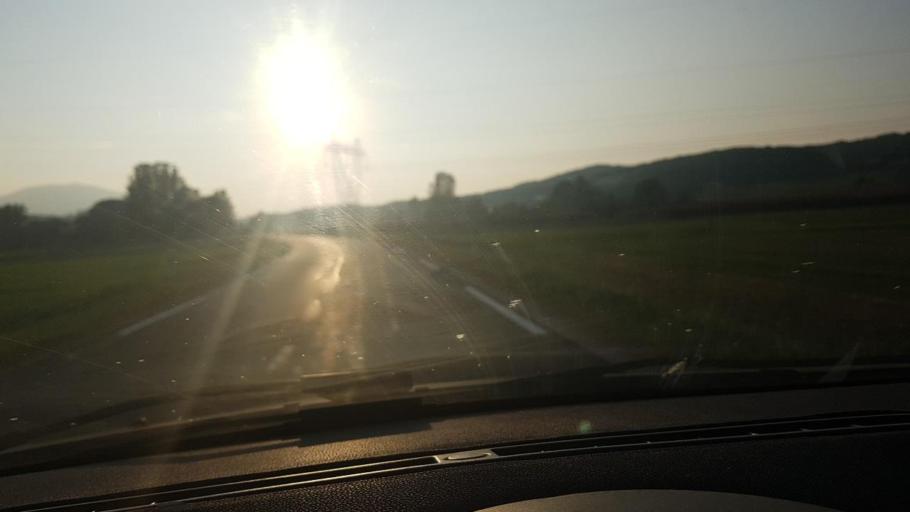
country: SI
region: Majsperk
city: Majsperk
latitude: 46.3386
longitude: 15.7157
